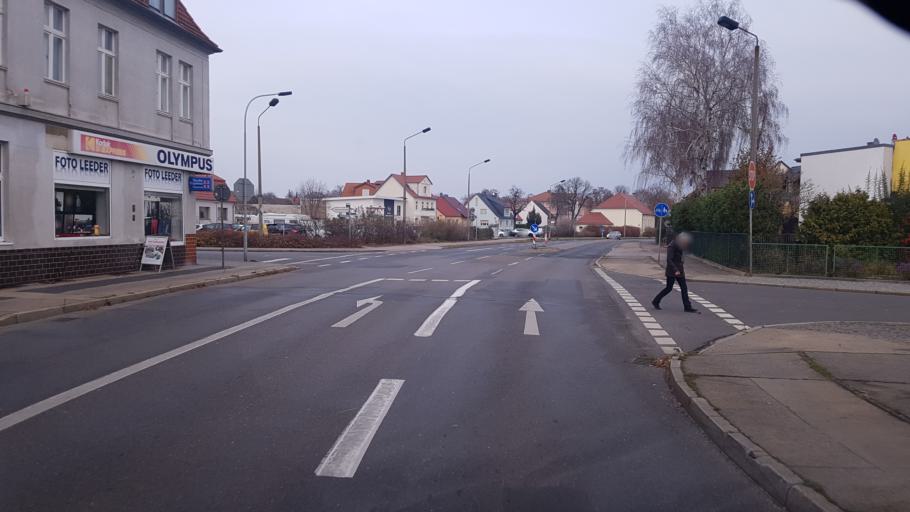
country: DE
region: Brandenburg
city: Eisenhuettenstadt
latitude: 52.1445
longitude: 14.6694
